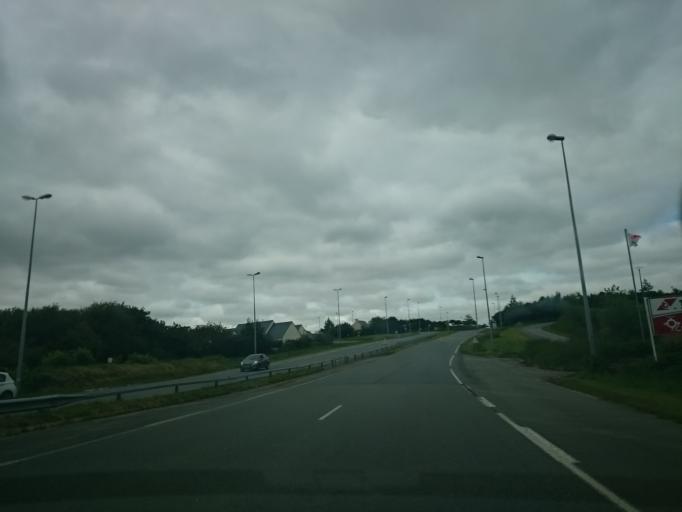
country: FR
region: Brittany
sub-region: Departement du Finistere
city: Gouesnou
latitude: 48.4398
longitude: -4.4655
